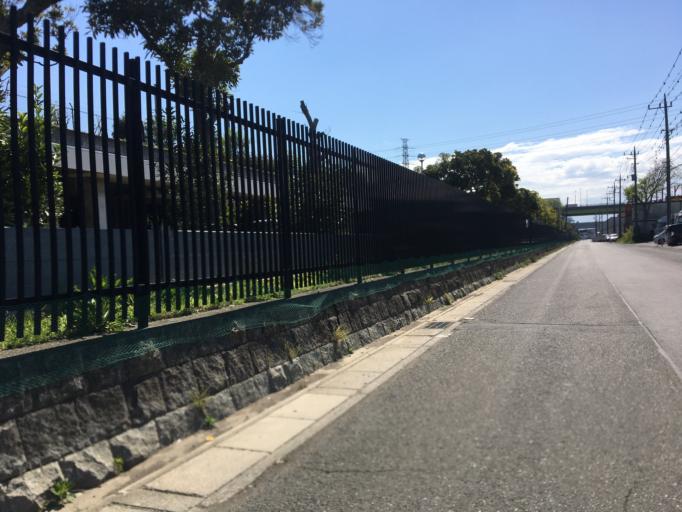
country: JP
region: Saitama
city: Asaka
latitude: 35.8047
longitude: 139.6176
